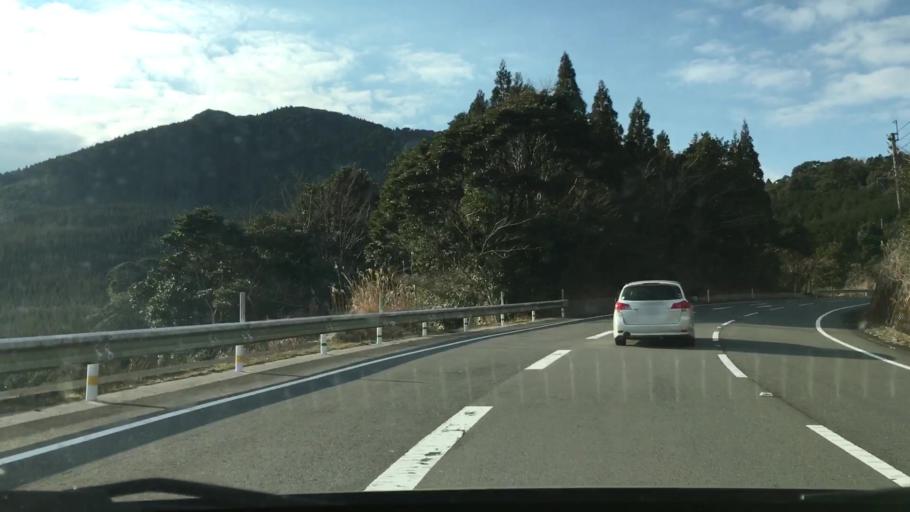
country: JP
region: Miyazaki
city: Miyazaki-shi
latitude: 31.7802
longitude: 131.3251
